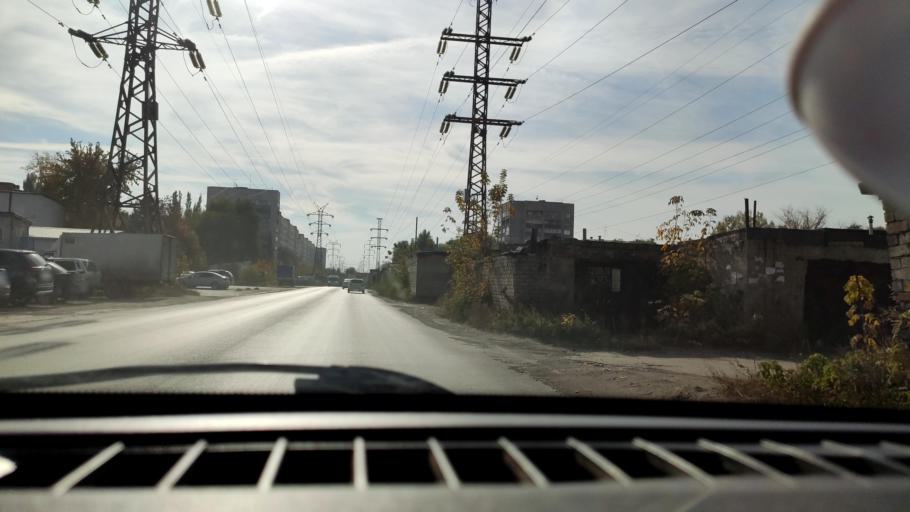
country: RU
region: Samara
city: Petra-Dubrava
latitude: 53.2403
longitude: 50.2885
